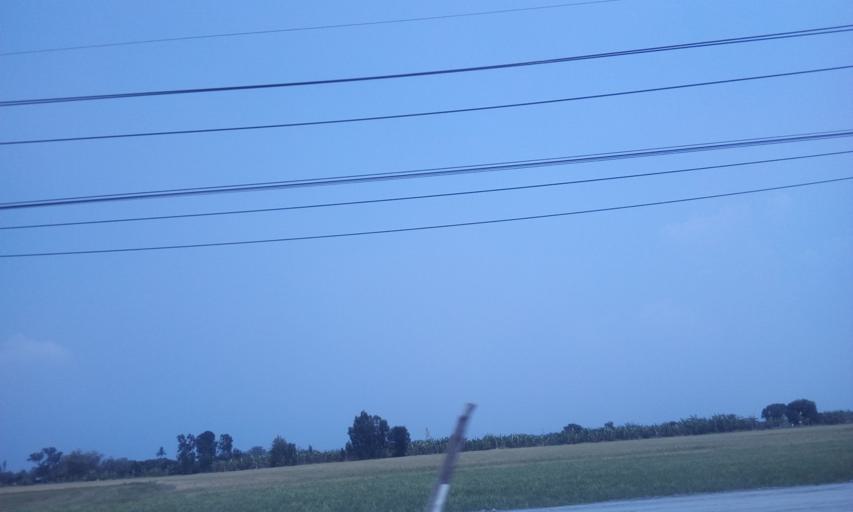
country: TH
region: Chon Buri
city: Phan Thong
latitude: 13.5370
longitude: 101.1483
